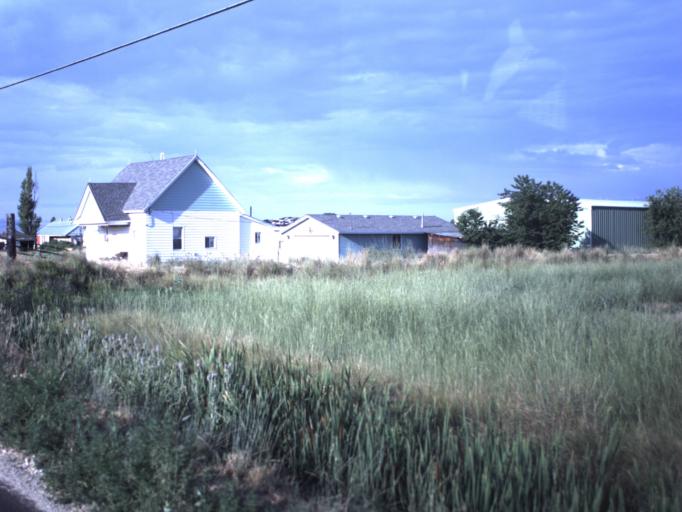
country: US
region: Utah
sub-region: Weber County
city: Plain City
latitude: 41.2528
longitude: -112.0926
